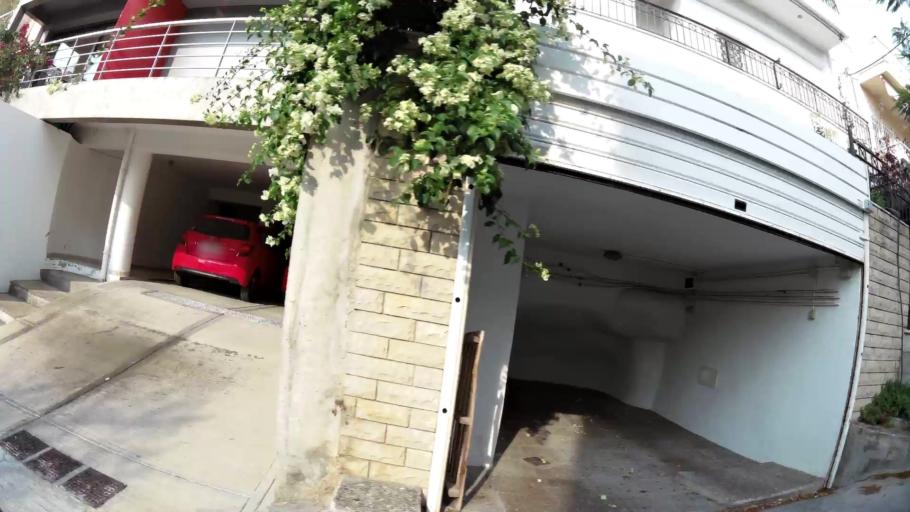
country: GR
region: Attica
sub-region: Nomarchia Athinas
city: Psychiko
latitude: 37.9980
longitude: 23.7598
